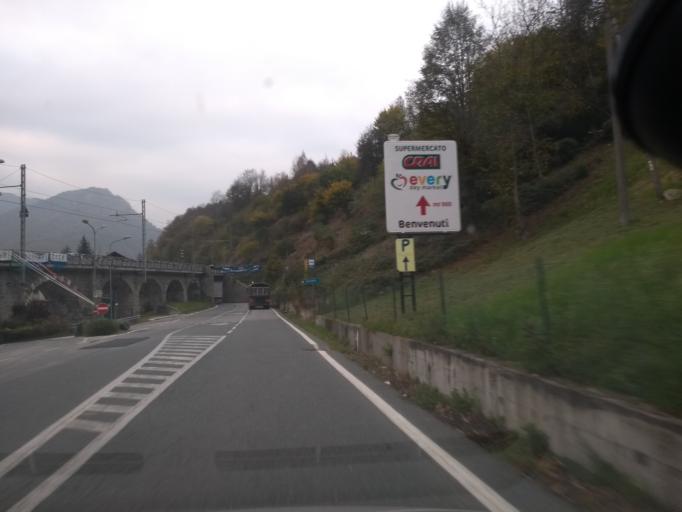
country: IT
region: Piedmont
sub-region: Provincia di Torino
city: Mezzenile
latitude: 45.2981
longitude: 7.4012
